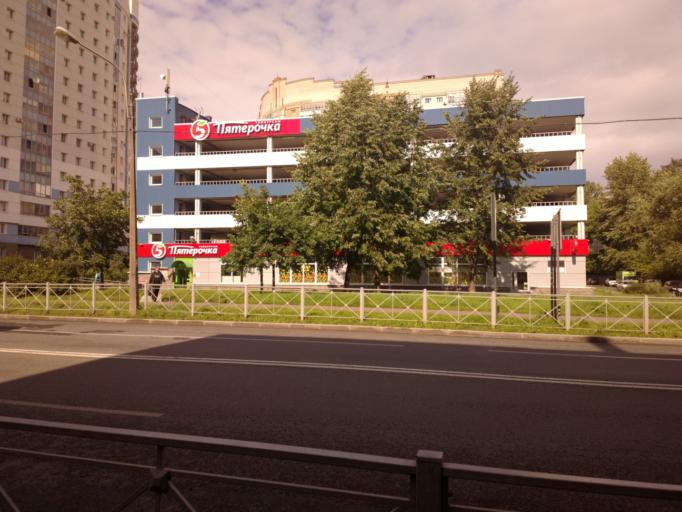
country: RU
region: St.-Petersburg
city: Vasyl'evsky Ostrov
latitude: 59.9442
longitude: 30.2378
